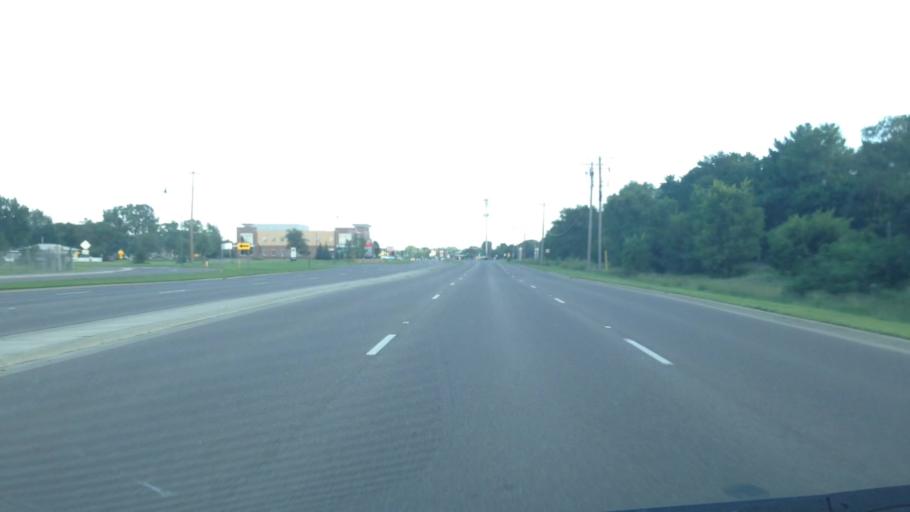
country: US
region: Minnesota
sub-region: Hennepin County
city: Crystal
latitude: 45.0591
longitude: -93.3615
